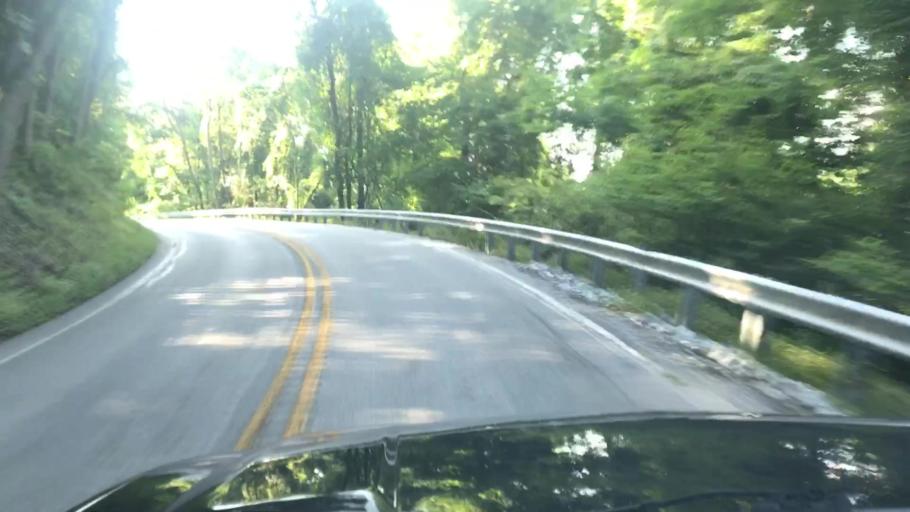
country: US
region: Pennsylvania
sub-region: York County
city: Valley Green
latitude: 40.1509
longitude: -76.8358
